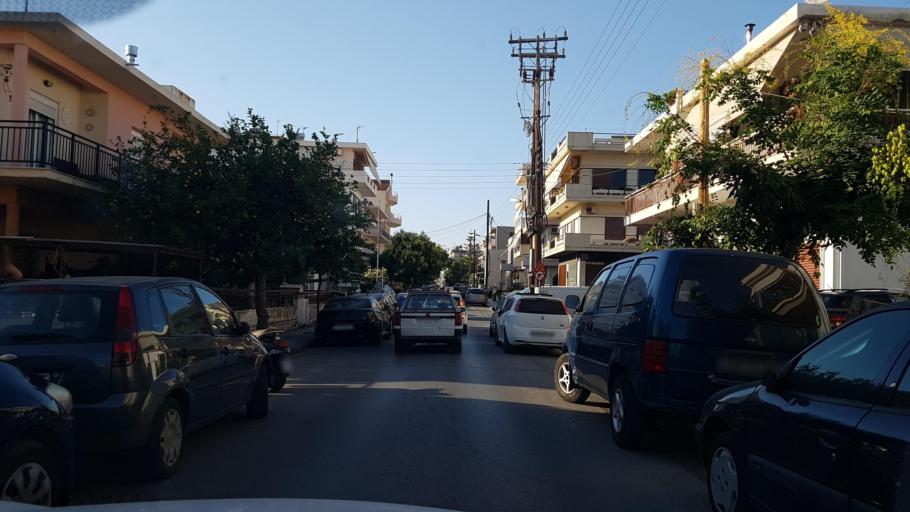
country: GR
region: Crete
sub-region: Nomos Chanias
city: Chania
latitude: 35.5080
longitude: 24.0141
